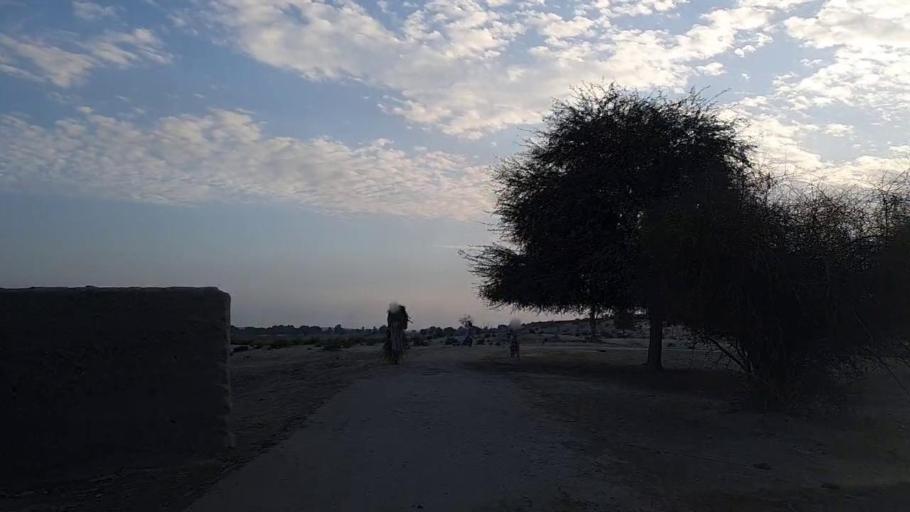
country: PK
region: Sindh
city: Daur
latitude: 26.4171
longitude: 68.4945
